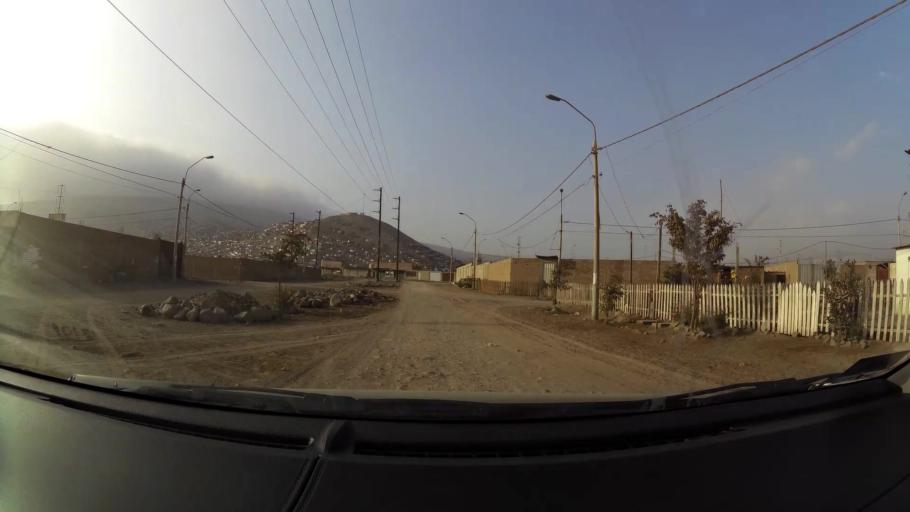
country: PE
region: Lima
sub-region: Lima
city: Santa Rosa
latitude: -11.7480
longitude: -77.1498
